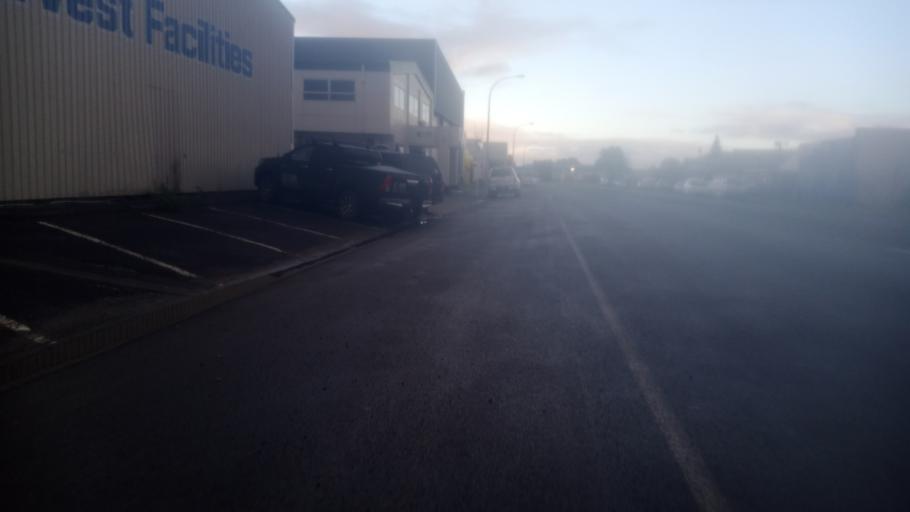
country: NZ
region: Gisborne
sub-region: Gisborne District
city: Gisborne
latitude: -38.6663
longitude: 177.9960
